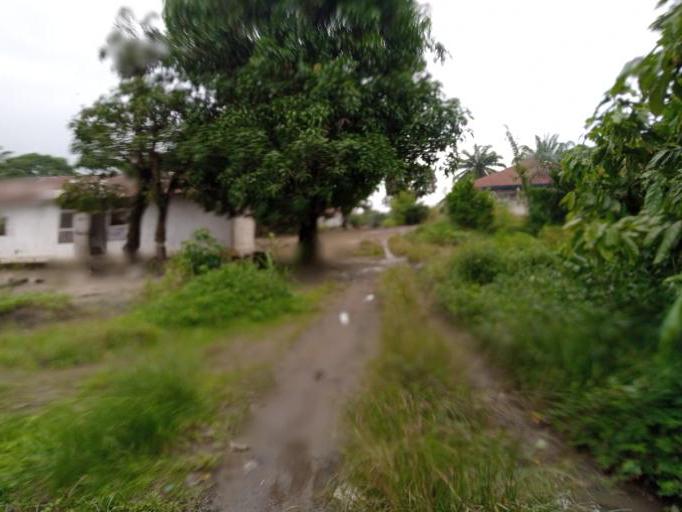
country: SL
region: Eastern Province
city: Kenema
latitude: 7.8575
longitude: -11.1985
